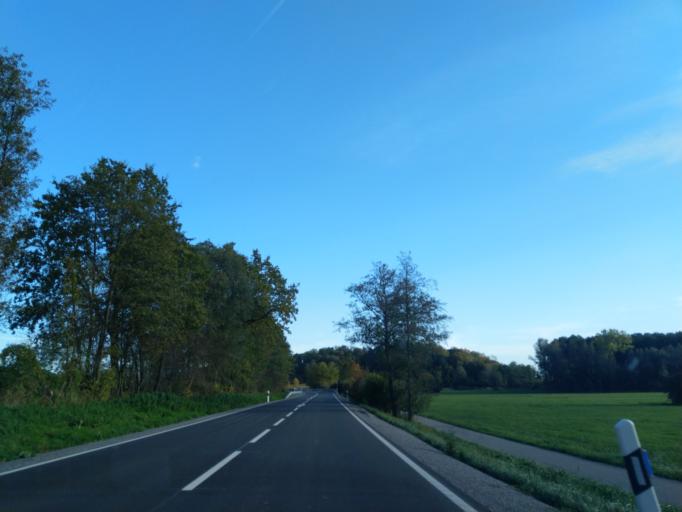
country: DE
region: Bavaria
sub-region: Lower Bavaria
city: Offenberg
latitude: 48.8682
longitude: 12.8587
